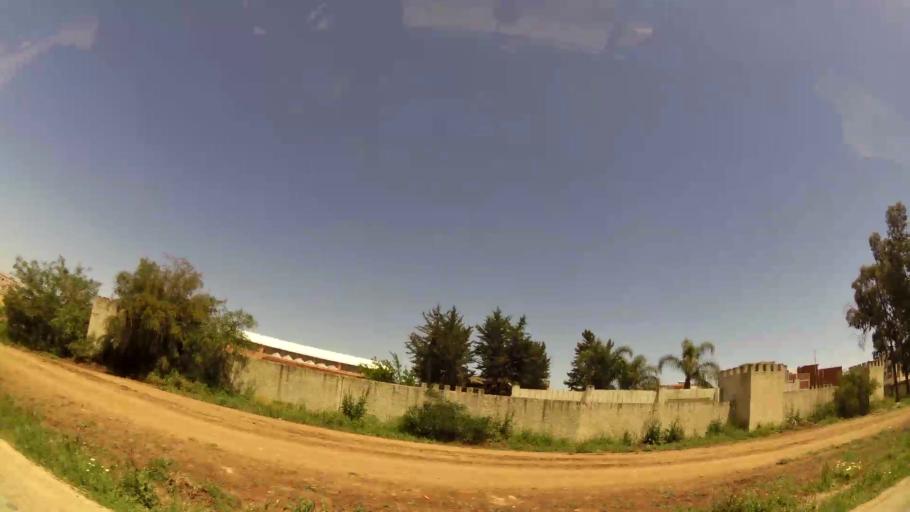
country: MA
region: Meknes-Tafilalet
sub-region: Meknes
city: Meknes
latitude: 33.8552
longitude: -5.5720
